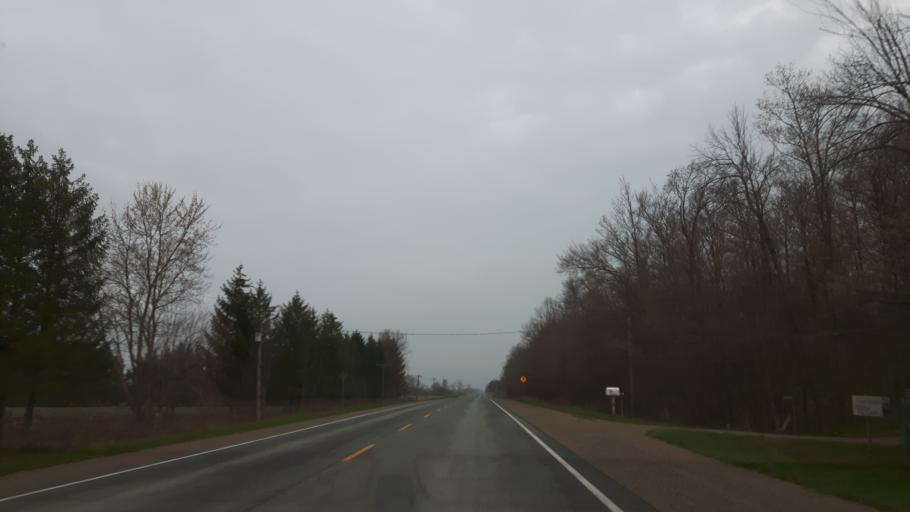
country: CA
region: Ontario
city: Bluewater
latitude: 43.5412
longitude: -81.6908
